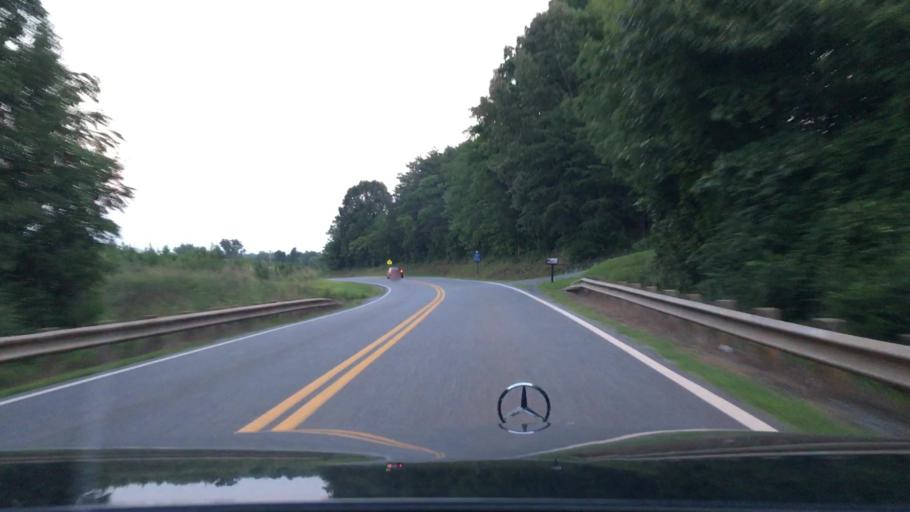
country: US
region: Virginia
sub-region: Campbell County
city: Altavista
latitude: 37.1332
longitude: -79.2874
